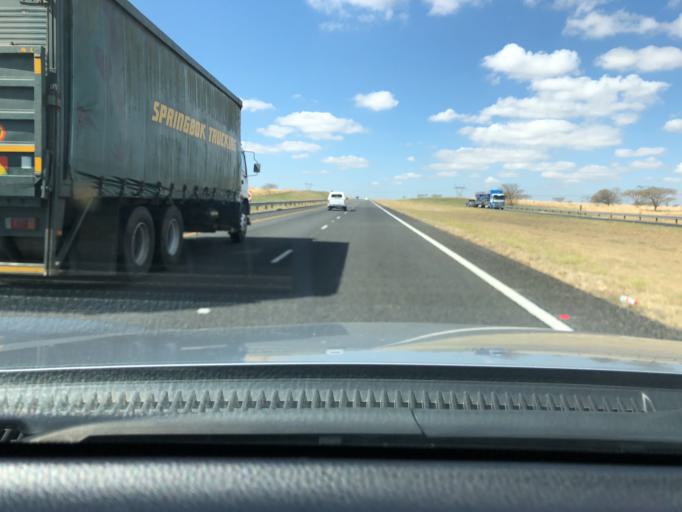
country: ZA
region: KwaZulu-Natal
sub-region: uThukela District Municipality
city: Estcourt
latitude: -28.8595
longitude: 29.7282
